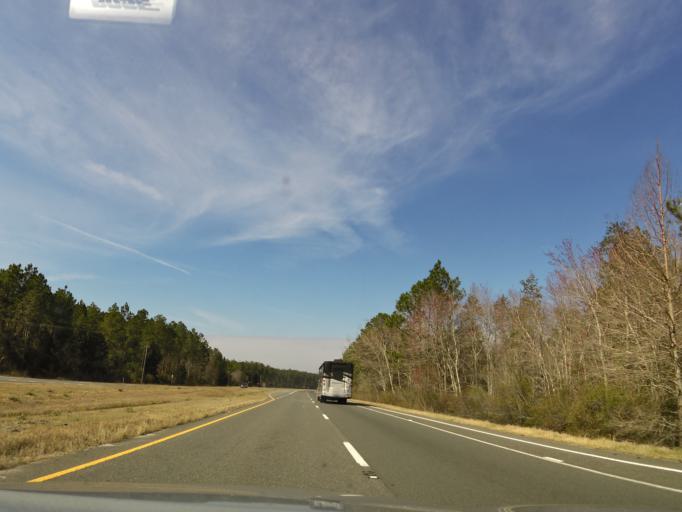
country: US
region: Georgia
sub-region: Ware County
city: Waycross
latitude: 31.1470
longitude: -82.2806
